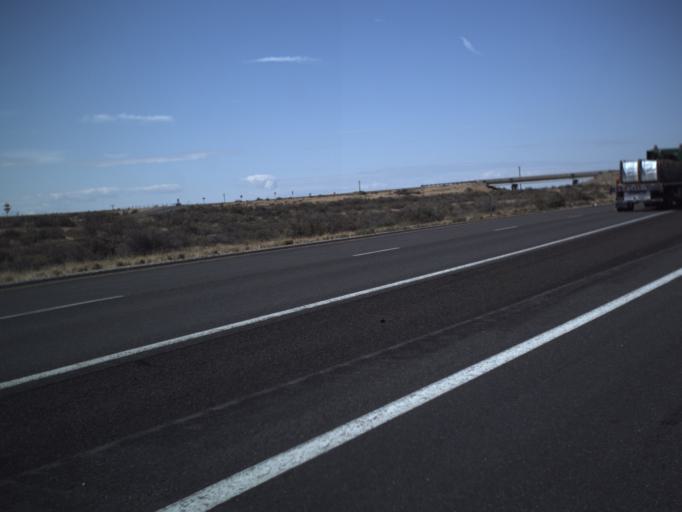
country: US
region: Utah
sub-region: Tooele County
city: Grantsville
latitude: 40.7340
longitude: -113.1082
